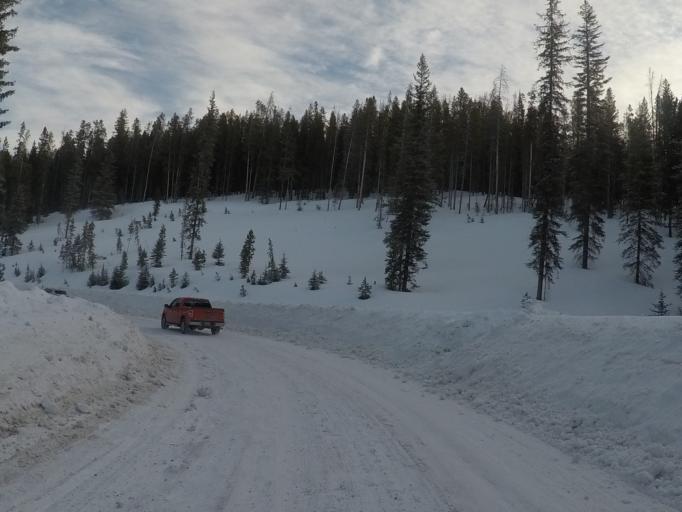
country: US
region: Montana
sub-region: Granite County
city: Philipsburg
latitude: 46.2385
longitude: -113.2432
